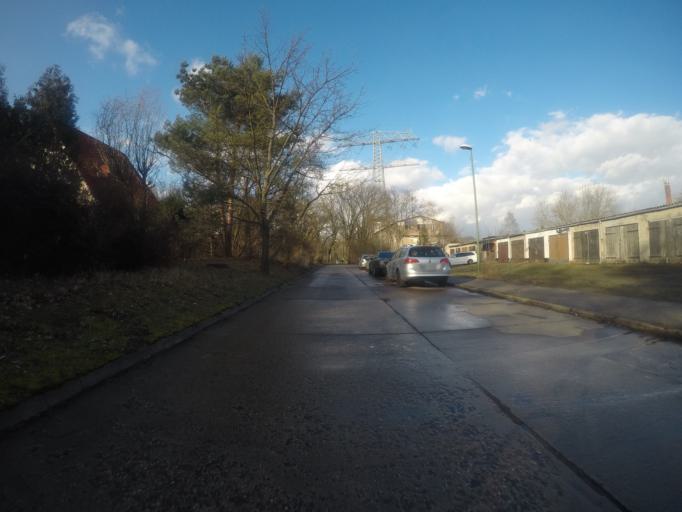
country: DE
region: Berlin
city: Karlshorst
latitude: 52.4968
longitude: 13.5403
